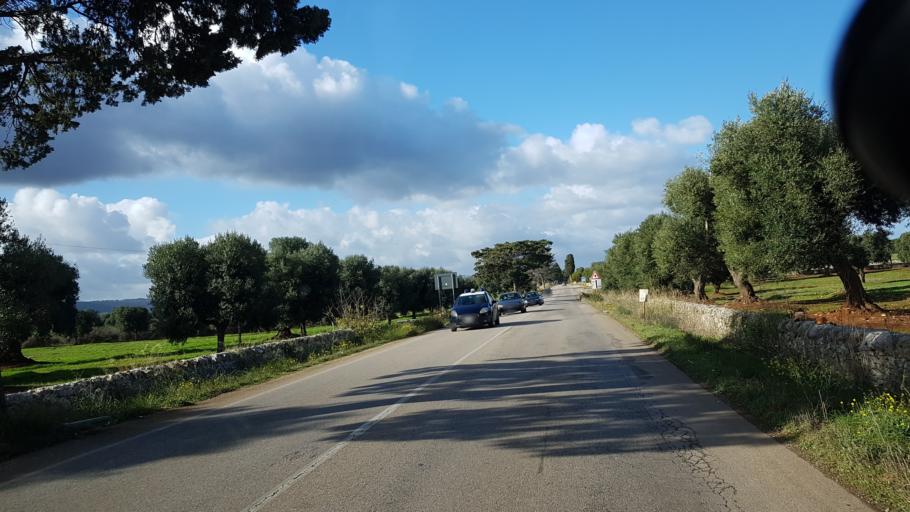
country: IT
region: Apulia
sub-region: Provincia di Brindisi
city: Pezze di Greco
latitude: 40.7984
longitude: 17.4448
